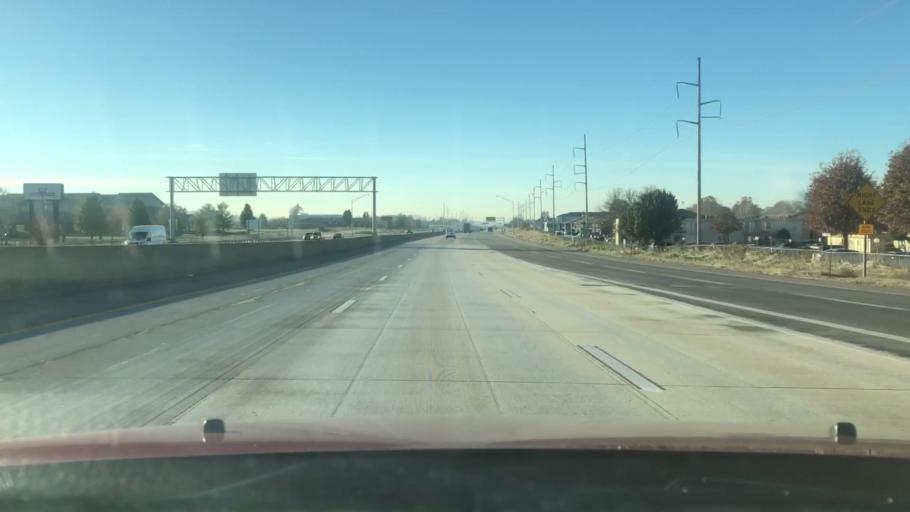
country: US
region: Missouri
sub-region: Greene County
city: Springfield
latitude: 37.1773
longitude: -93.2244
